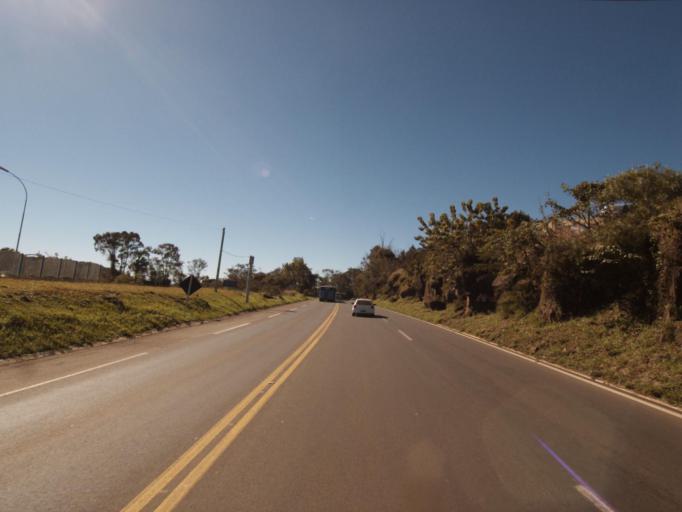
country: BR
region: Santa Catarina
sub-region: Chapeco
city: Chapeco
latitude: -26.9859
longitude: -52.6046
